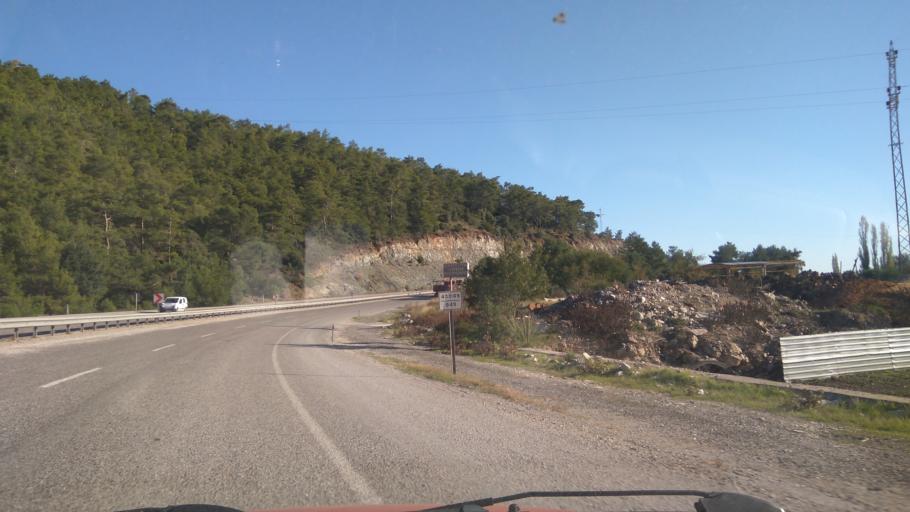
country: TR
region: Antalya
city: Kemer
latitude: 36.5819
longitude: 30.5532
